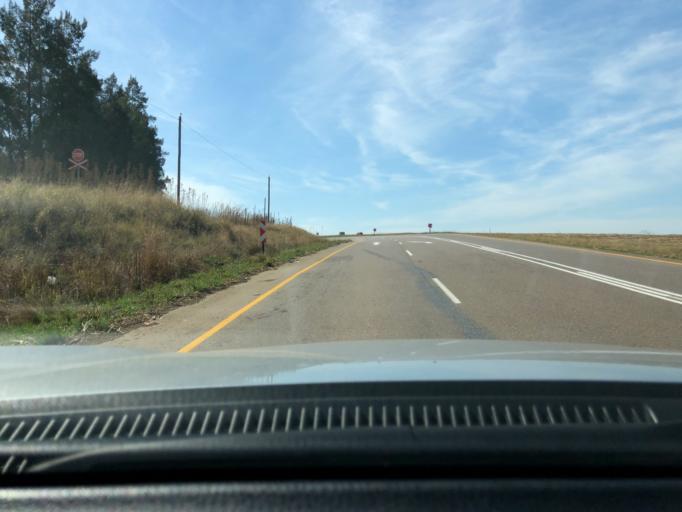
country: ZA
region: KwaZulu-Natal
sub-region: uMgungundlovu District Municipality
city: Richmond
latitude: -29.7954
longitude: 30.3476
